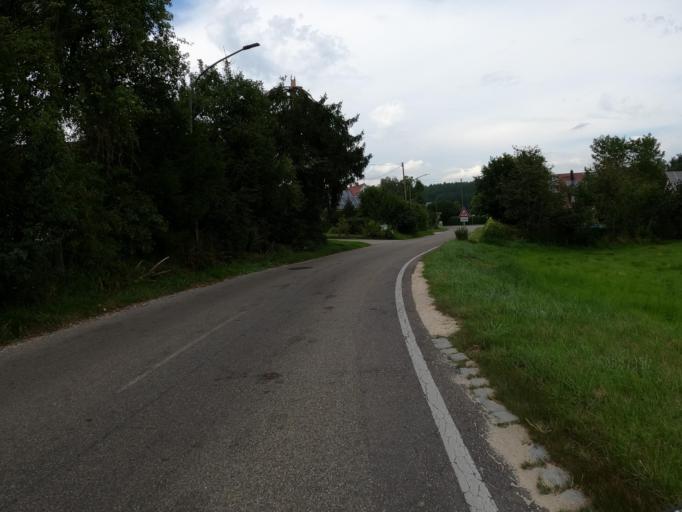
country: DE
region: Bavaria
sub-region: Swabia
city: Pfaffenhofen an der Roth
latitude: 48.3586
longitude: 10.2068
